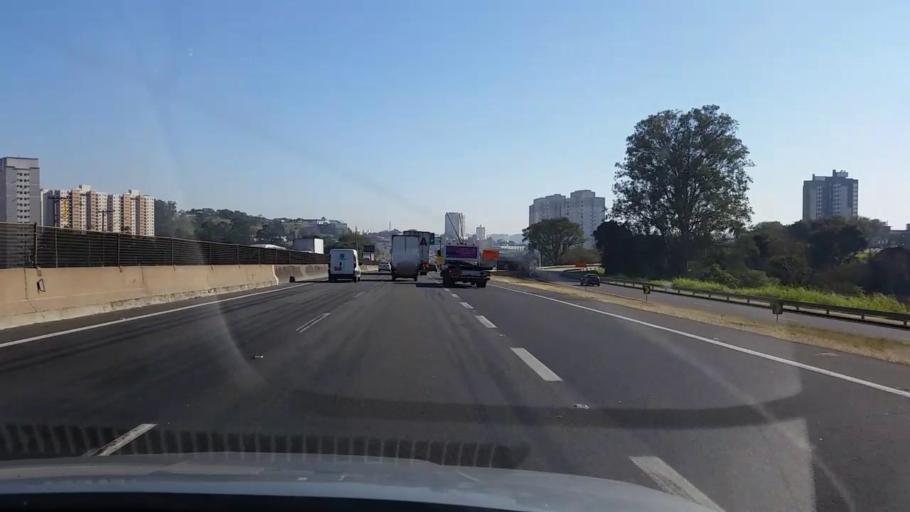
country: BR
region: Sao Paulo
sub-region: Jundiai
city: Jundiai
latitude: -23.1947
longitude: -46.9045
